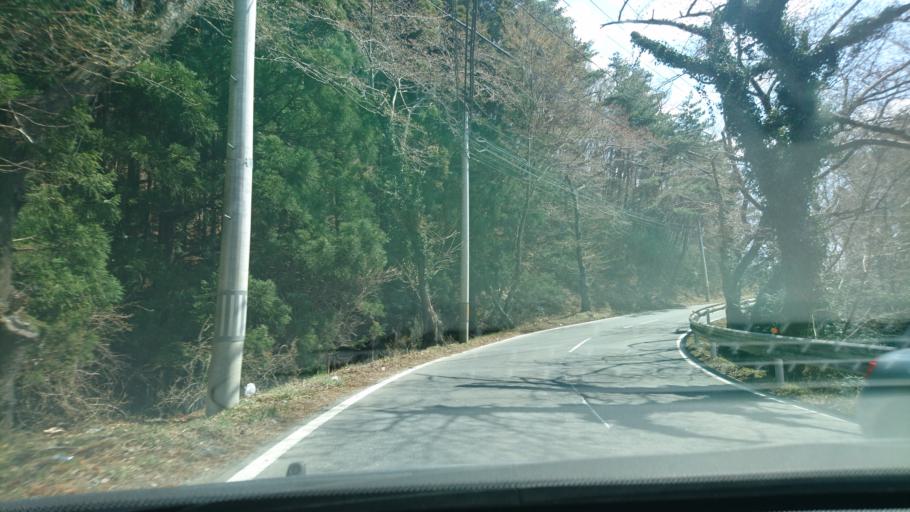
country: JP
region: Miyagi
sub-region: Oshika Gun
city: Onagawa Cho
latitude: 38.4402
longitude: 141.4810
